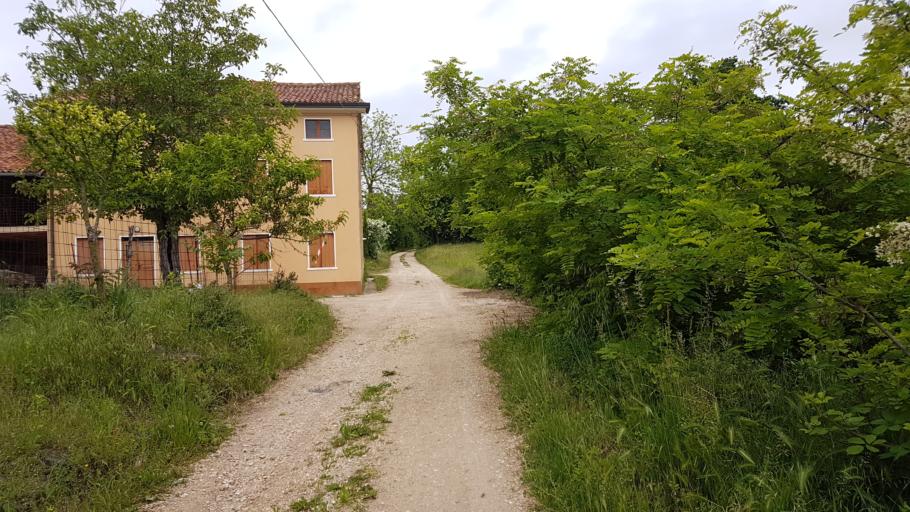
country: IT
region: Veneto
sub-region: Provincia di Vicenza
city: Trissino
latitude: 45.5583
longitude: 11.3369
